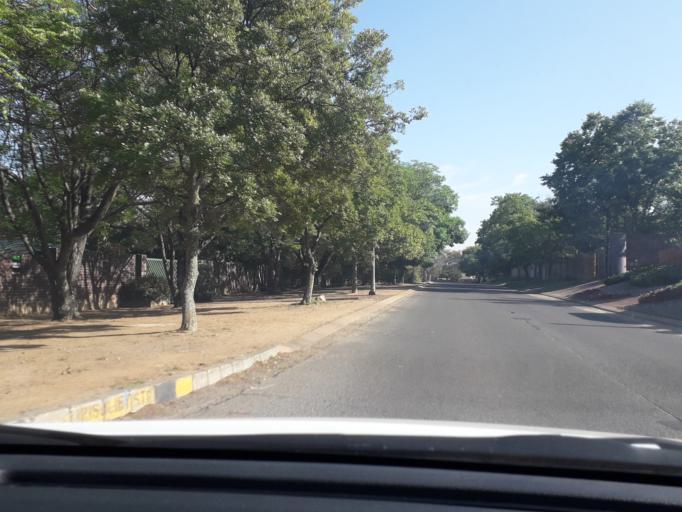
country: ZA
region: Gauteng
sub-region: City of Johannesburg Metropolitan Municipality
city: Diepsloot
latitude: -26.0302
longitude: 27.9882
